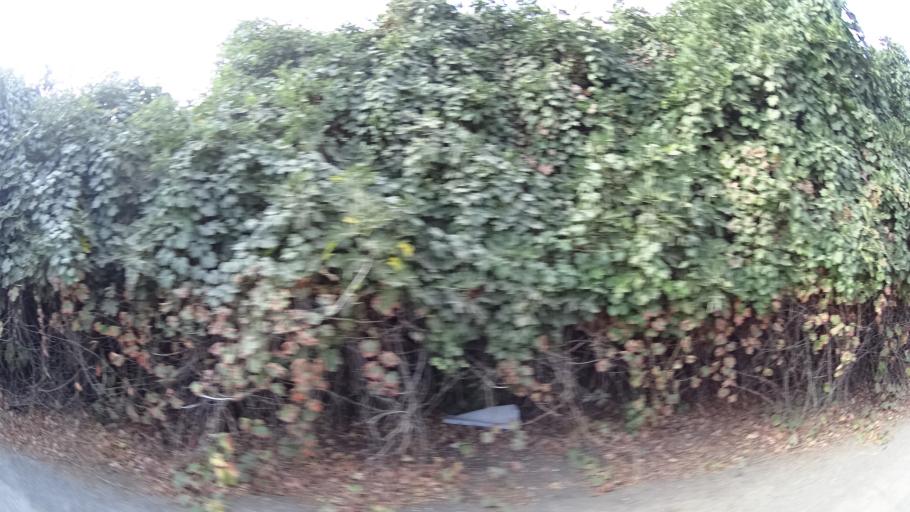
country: US
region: California
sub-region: Yolo County
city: Woodland
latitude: 38.7592
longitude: -121.6778
